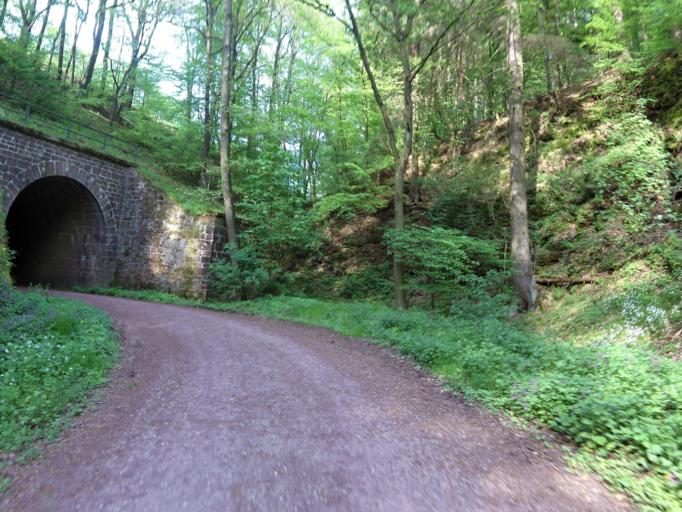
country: DE
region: Thuringia
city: Eisenach
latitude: 50.9647
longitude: 10.2933
